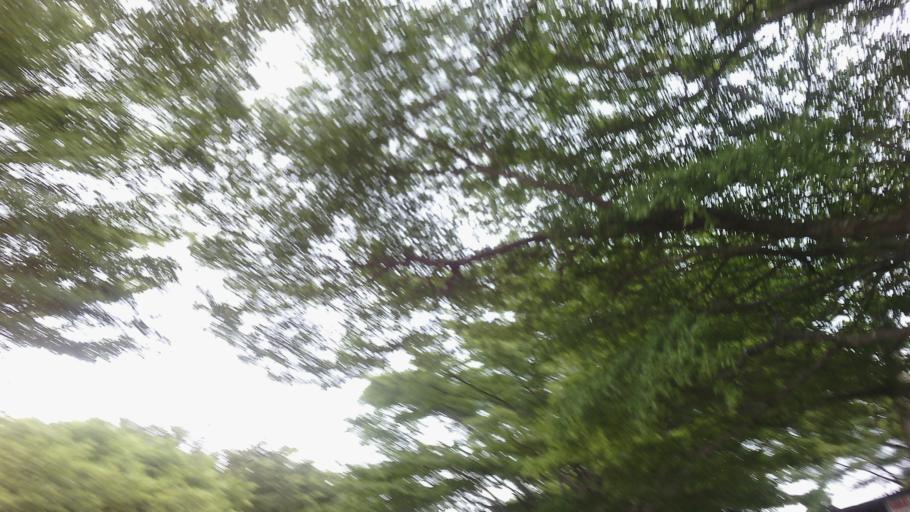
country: BJ
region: Atlantique
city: Abomey-Calavi
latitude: 6.4756
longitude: 2.3562
